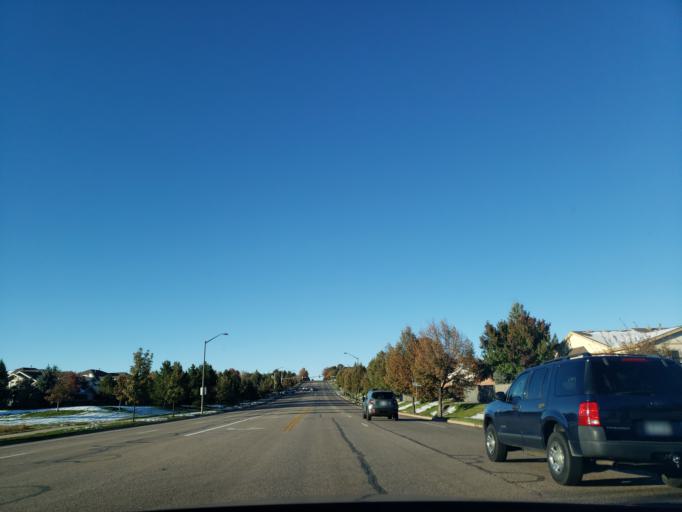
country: US
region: Colorado
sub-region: Larimer County
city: Fort Collins
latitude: 40.5069
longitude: -105.0581
